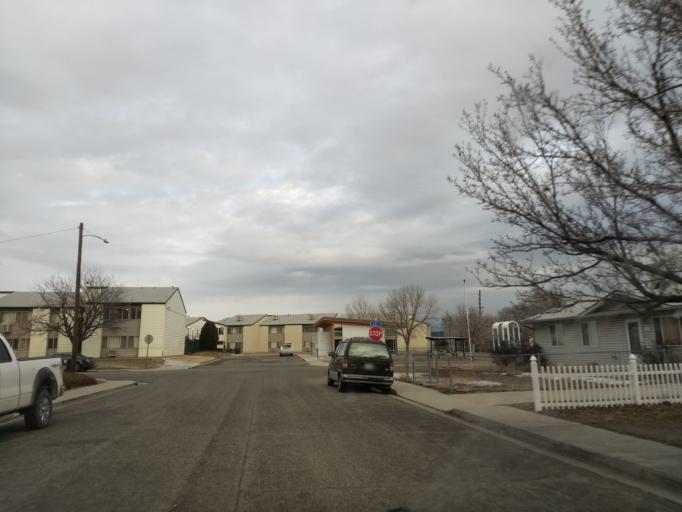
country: US
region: Colorado
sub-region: Mesa County
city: Grand Junction
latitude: 39.0742
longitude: -108.5357
